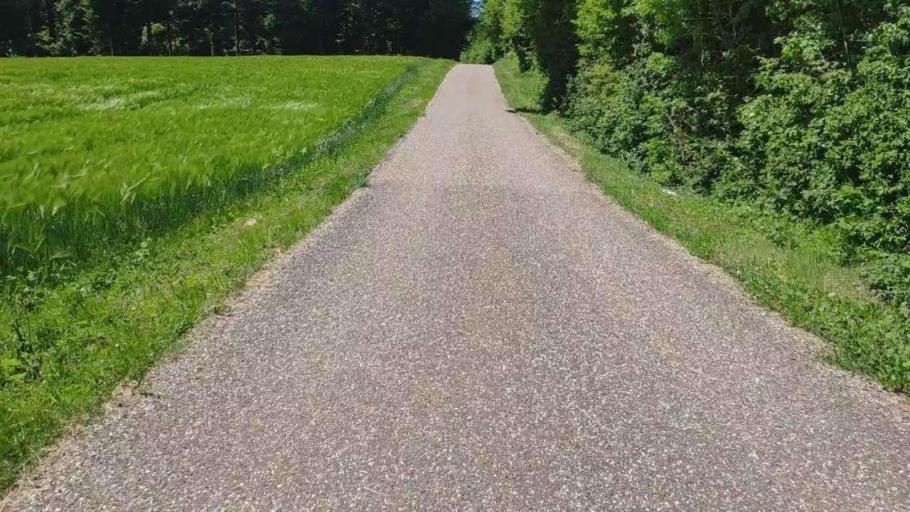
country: FR
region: Franche-Comte
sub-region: Departement du Jura
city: Poligny
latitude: 46.7336
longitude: 5.6791
